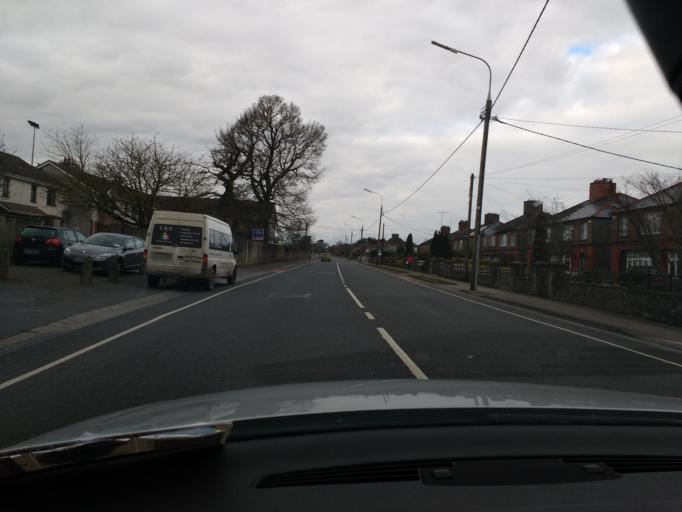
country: IE
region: Leinster
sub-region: Kilkenny
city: Kilkenny
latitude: 52.6600
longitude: -7.2592
